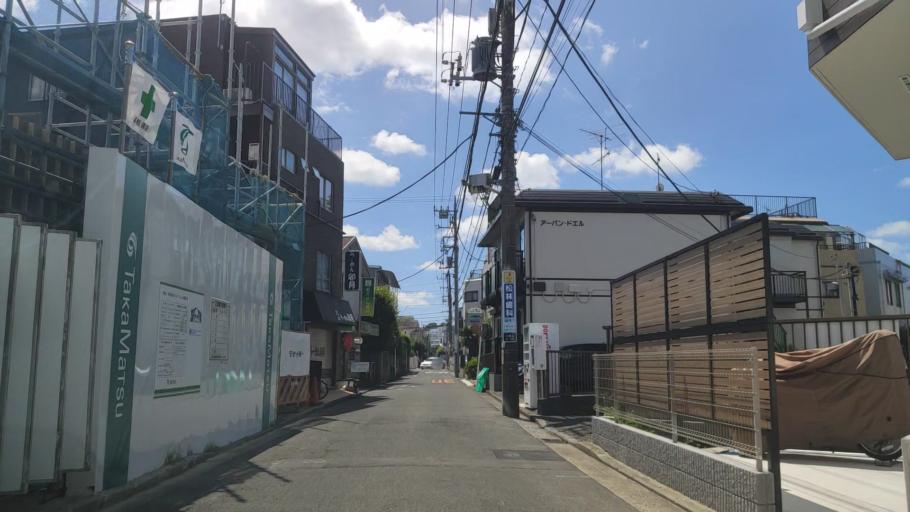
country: JP
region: Kanagawa
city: Yokohama
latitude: 35.5203
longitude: 139.6280
